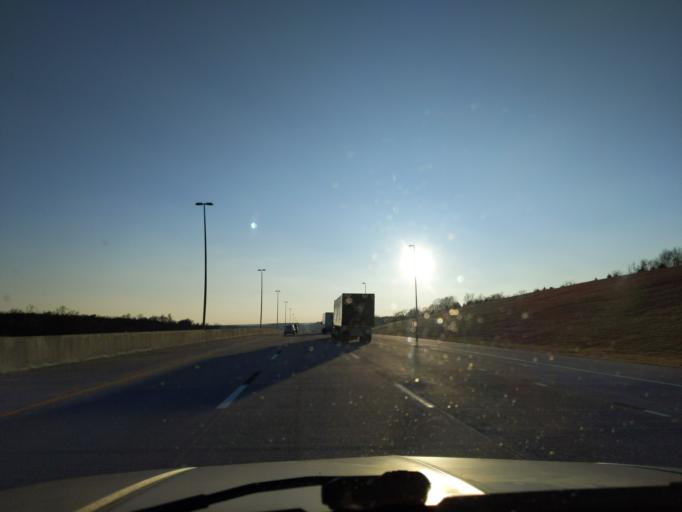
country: US
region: Oklahoma
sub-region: Creek County
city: Kellyville
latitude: 35.9824
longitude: -96.2012
